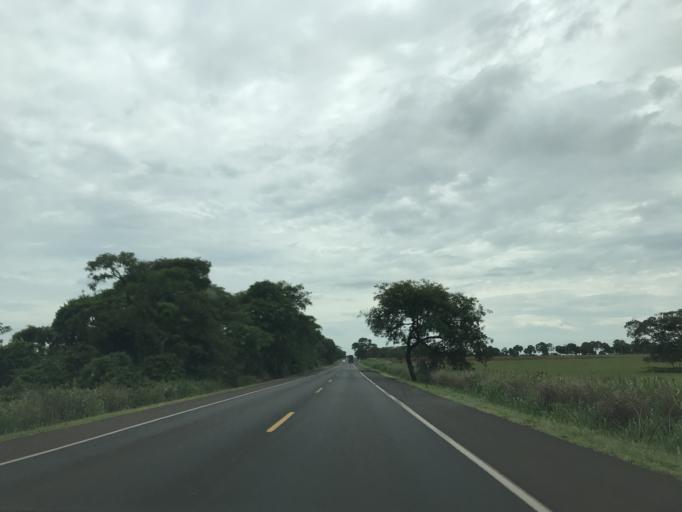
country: BR
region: Minas Gerais
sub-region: Frutal
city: Frutal
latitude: -20.2382
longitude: -49.1596
